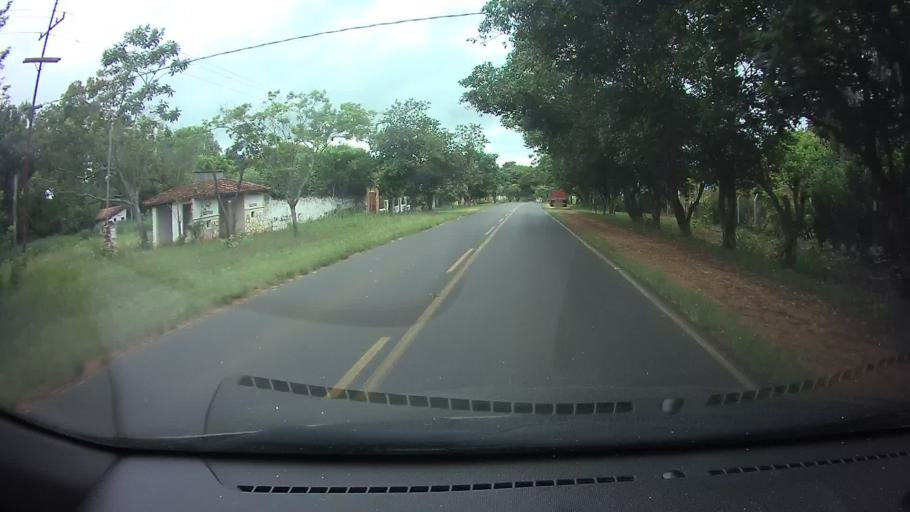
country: PY
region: Central
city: Guarambare
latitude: -25.5311
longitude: -57.4986
